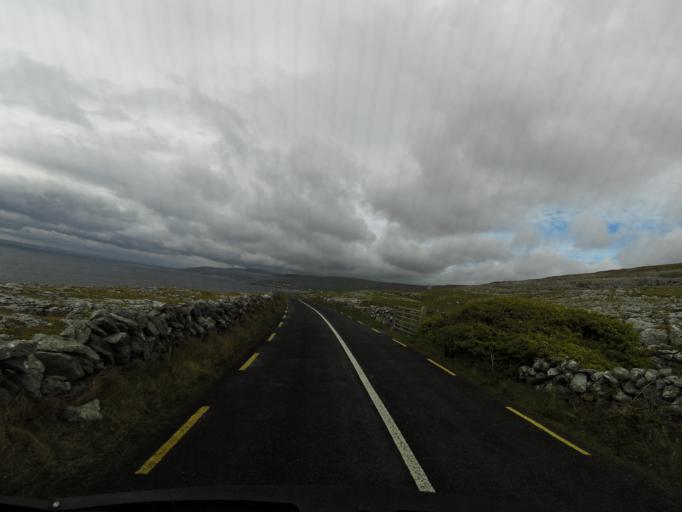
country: IE
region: Connaught
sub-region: County Galway
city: Bearna
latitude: 53.0770
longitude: -9.3430
